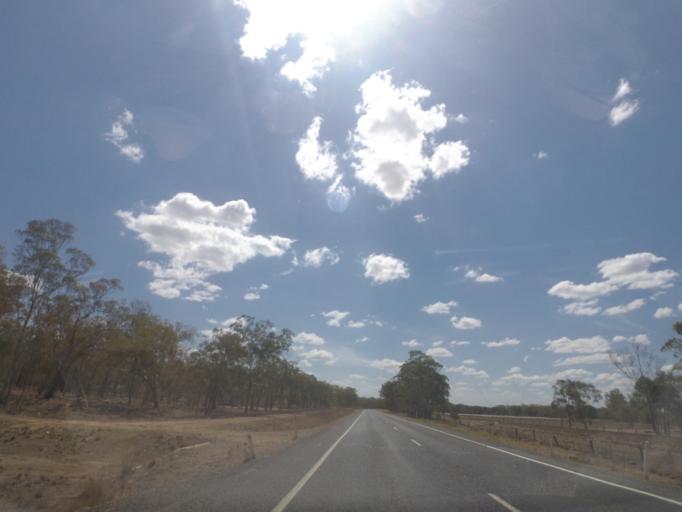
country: AU
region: Queensland
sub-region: Southern Downs
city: Warwick
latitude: -28.1633
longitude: 151.7125
